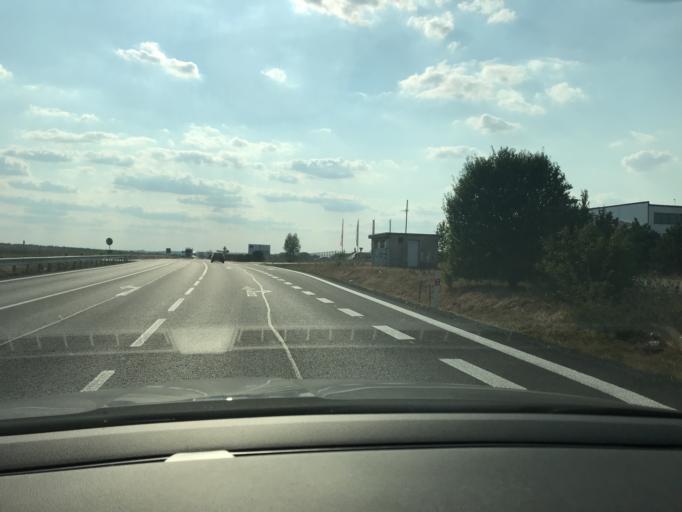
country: CZ
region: Central Bohemia
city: Velvary
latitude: 50.2722
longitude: 14.2258
